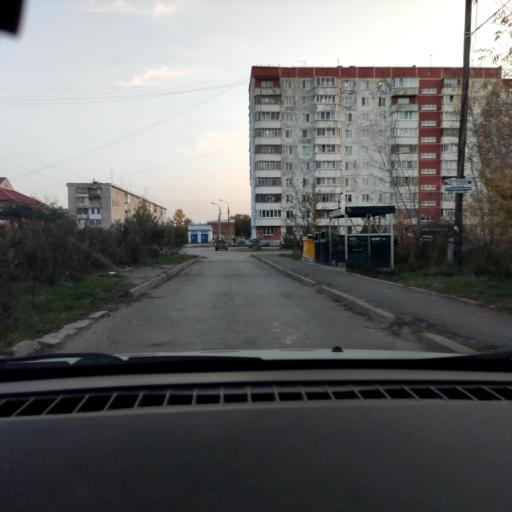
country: RU
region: Perm
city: Overyata
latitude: 58.0281
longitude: 55.8350
